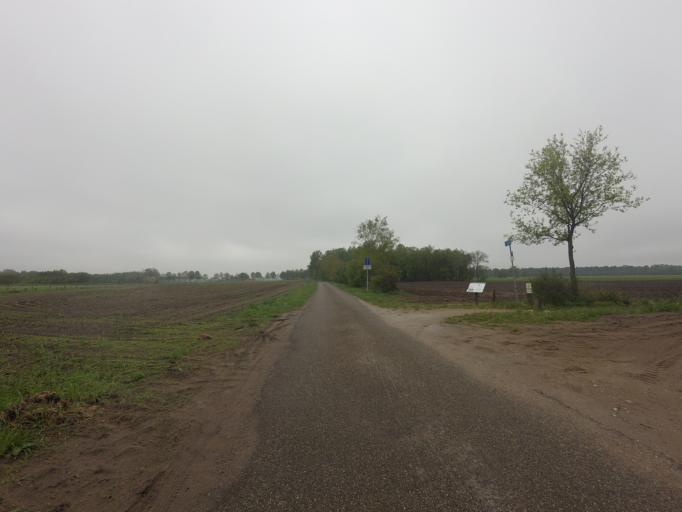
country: DE
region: North Rhine-Westphalia
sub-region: Regierungsbezirk Munster
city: Vreden
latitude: 52.1253
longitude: 6.8449
